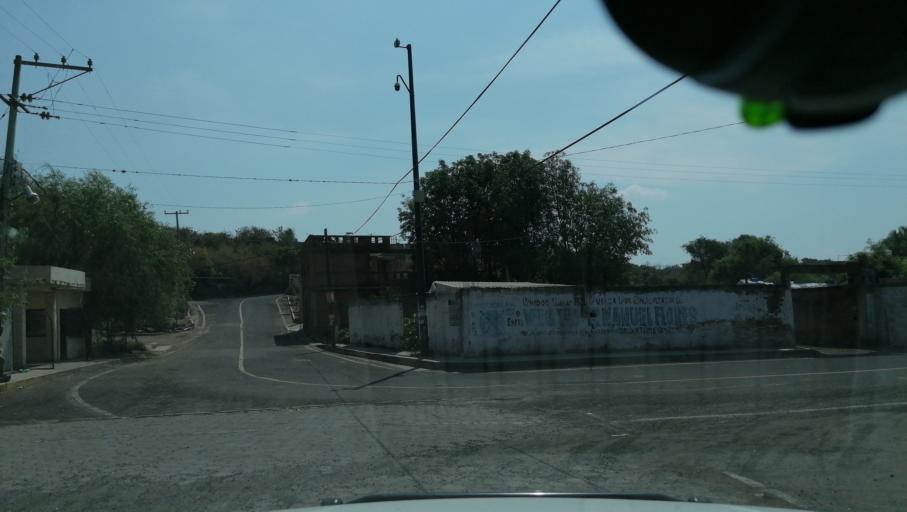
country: MX
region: Puebla
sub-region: Tianguismanalco
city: San Baltazar Atlimeyaya
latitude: 18.9856
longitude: -98.4793
